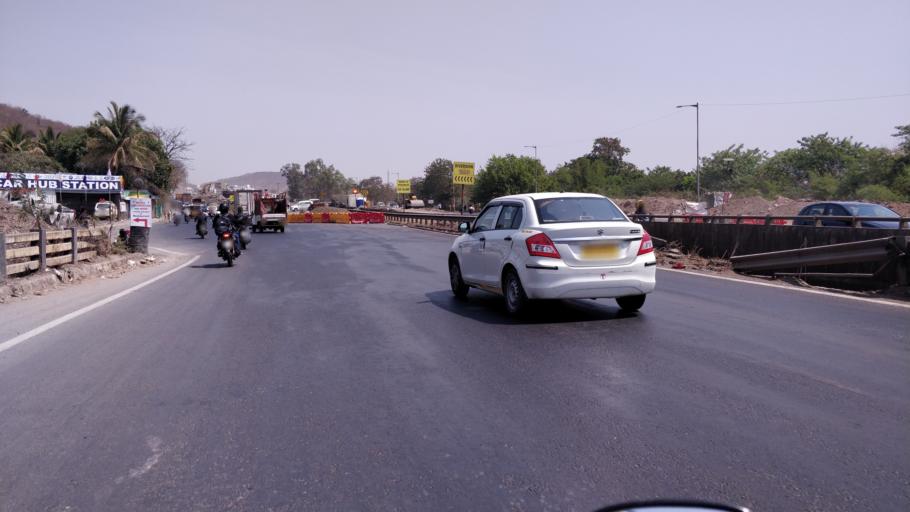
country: IN
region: Maharashtra
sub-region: Pune Division
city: Shivaji Nagar
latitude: 18.5314
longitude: 73.7794
